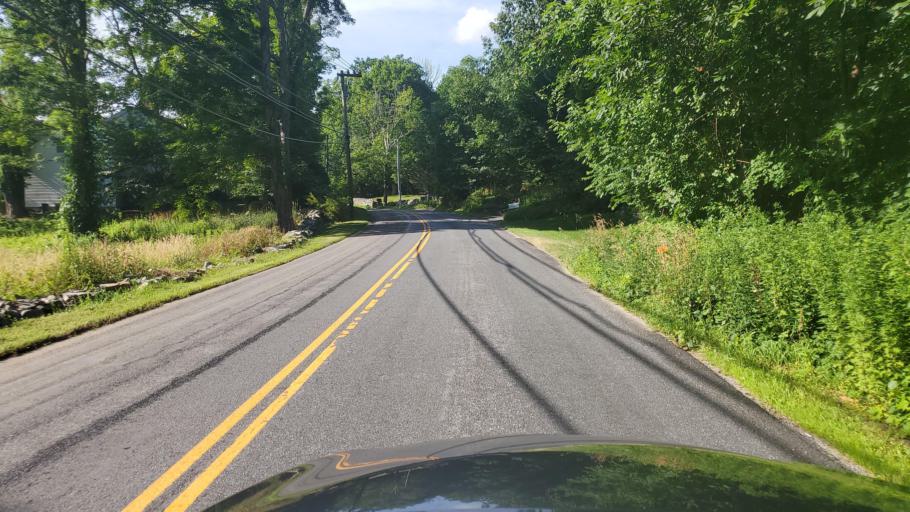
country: US
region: Connecticut
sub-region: Fairfield County
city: Newtown
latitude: 41.3818
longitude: -73.3134
